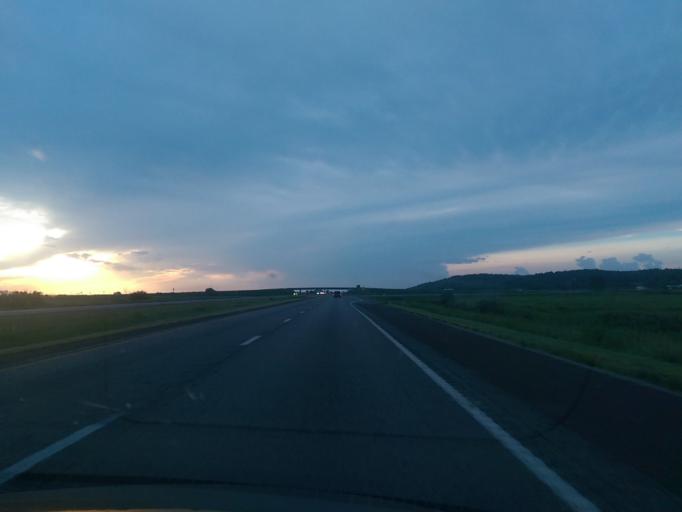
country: US
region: Missouri
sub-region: Atchison County
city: Rock Port
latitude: 40.2591
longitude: -95.4491
